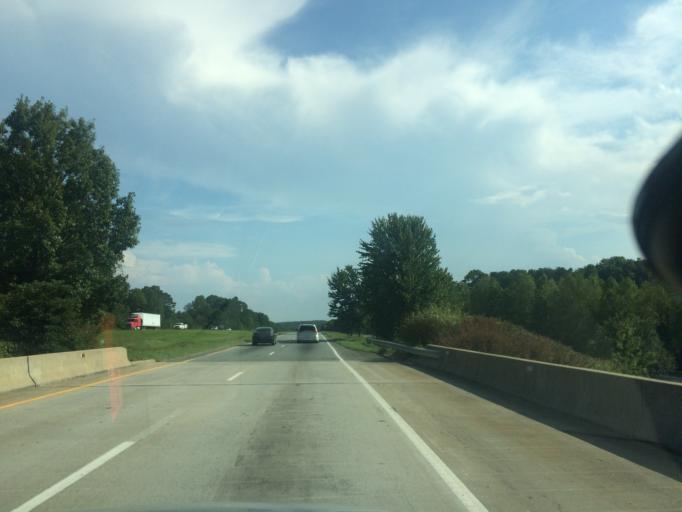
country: US
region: North Carolina
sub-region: Lincoln County
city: Lincolnton
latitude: 35.4160
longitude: -81.2112
